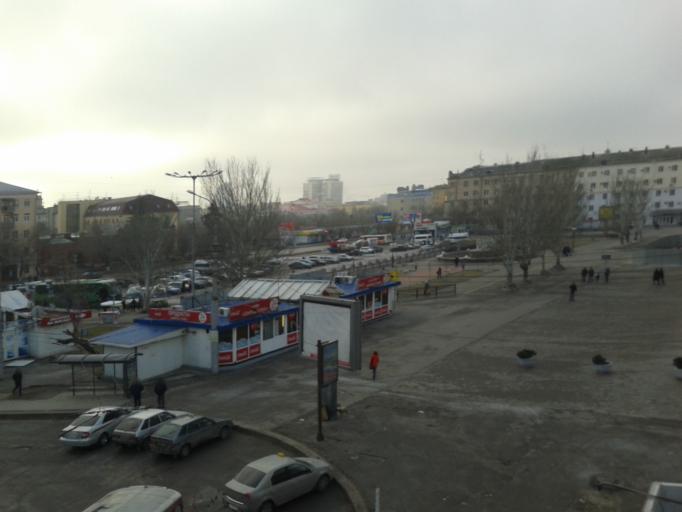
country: RU
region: Volgograd
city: Volgograd
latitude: 48.7131
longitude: 44.5147
